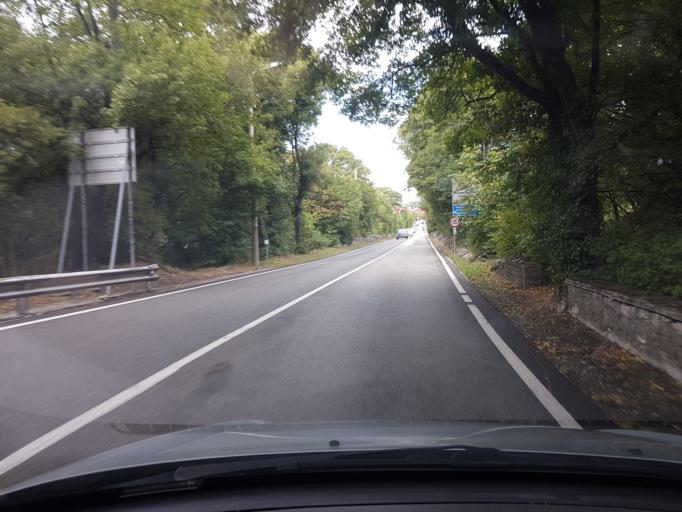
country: IT
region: Friuli Venezia Giulia
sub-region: Provincia di Trieste
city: Prosecco-Contovello
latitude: 45.7092
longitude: 13.7299
